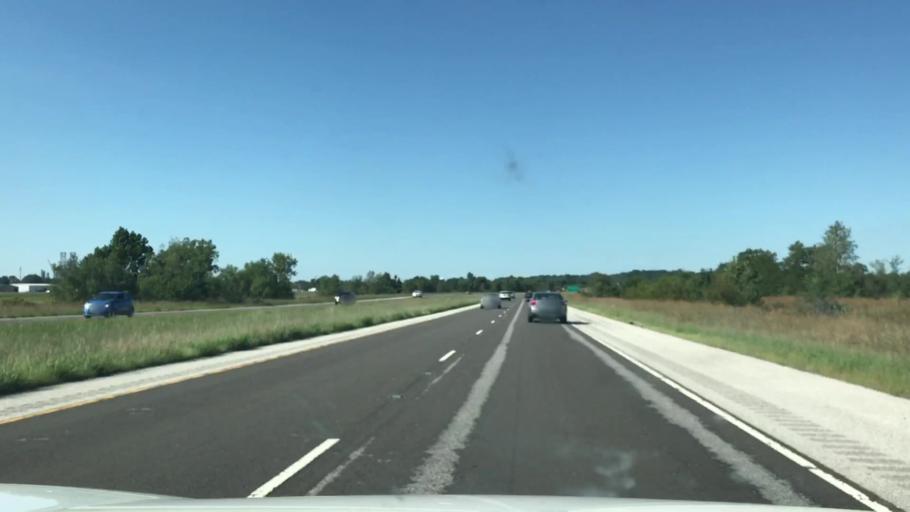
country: US
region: Illinois
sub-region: Madison County
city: South Roxana
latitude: 38.8225
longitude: -90.0428
